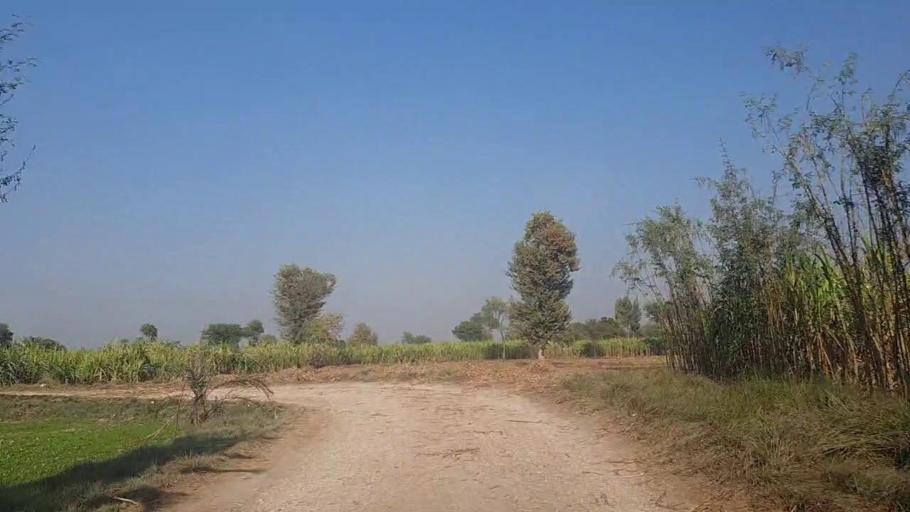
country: PK
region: Sindh
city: Gambat
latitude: 27.3671
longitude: 68.4750
